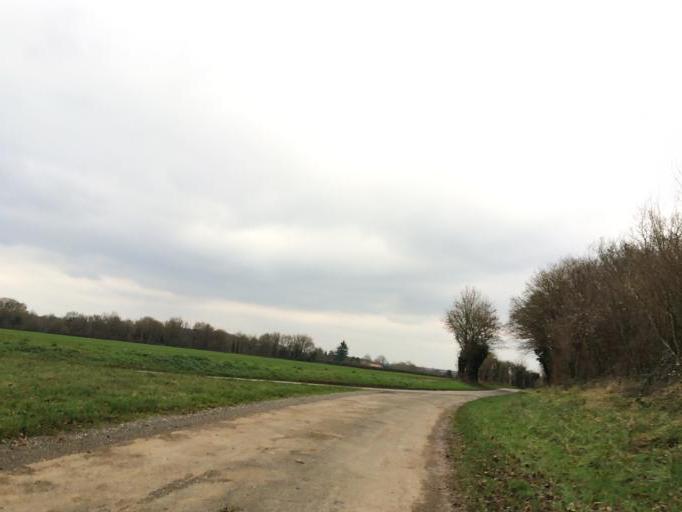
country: FR
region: Poitou-Charentes
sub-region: Departement des Deux-Sevres
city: Sauze-Vaussais
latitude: 46.1574
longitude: 0.1516
